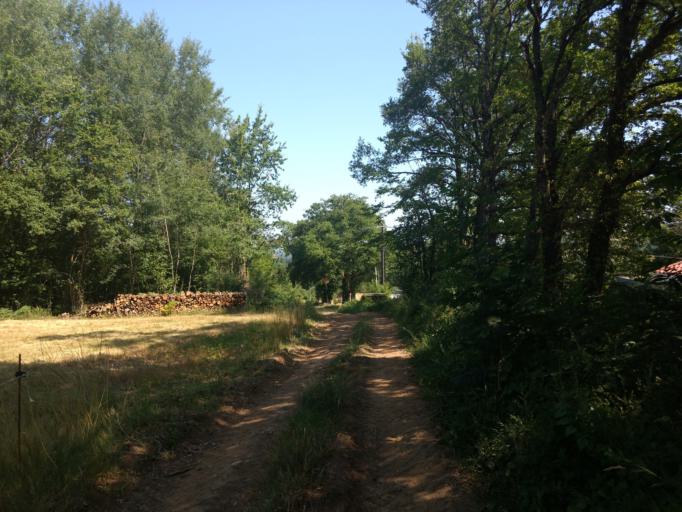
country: FR
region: Midi-Pyrenees
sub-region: Departement de l'Aveyron
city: Livinhac-le-Haut
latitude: 44.6070
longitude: 2.1593
